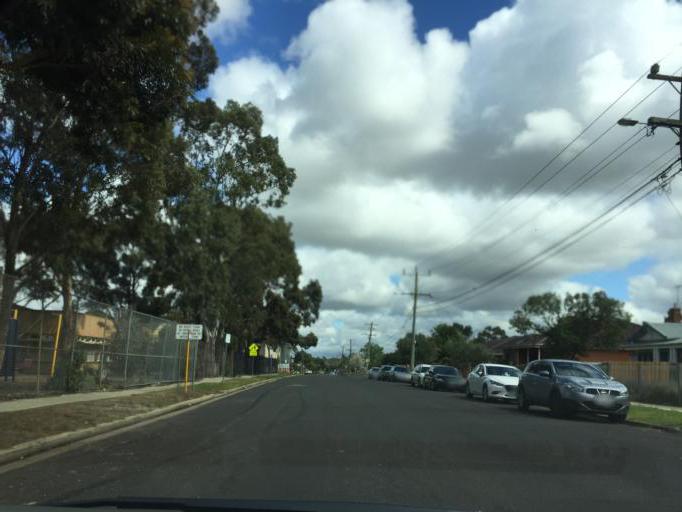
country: AU
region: Victoria
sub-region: Brimbank
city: Sunshine West
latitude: -37.7903
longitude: 144.8304
